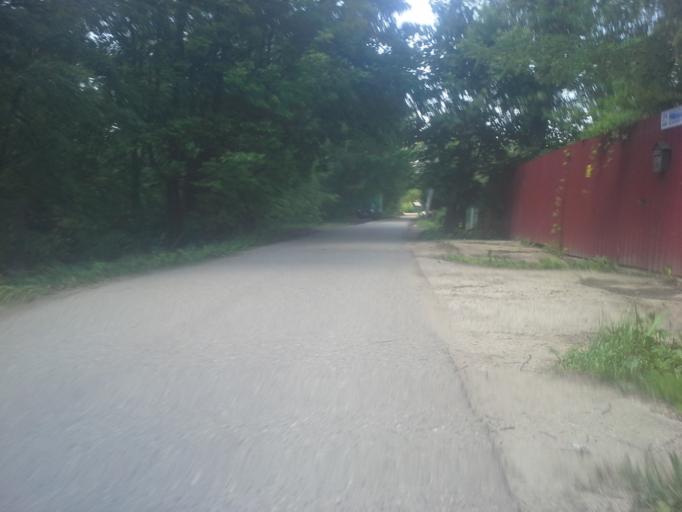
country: RU
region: Moskovskaya
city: Lesnoy Gorodok
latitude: 55.6651
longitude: 37.1808
